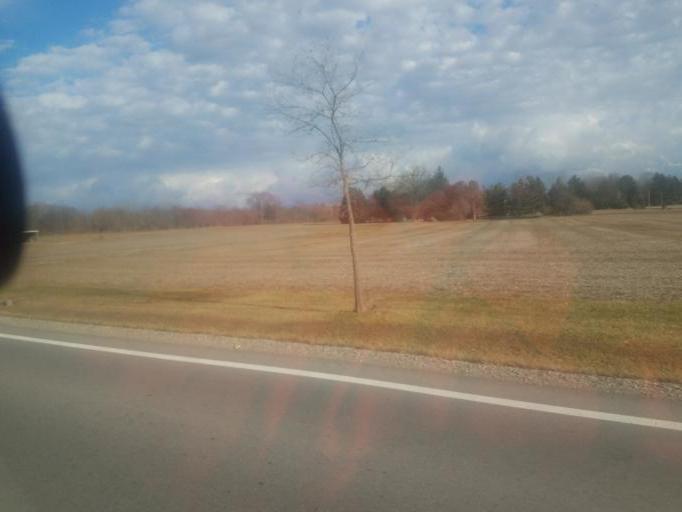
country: US
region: Ohio
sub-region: Marion County
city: Marion
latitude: 40.5006
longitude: -83.0642
